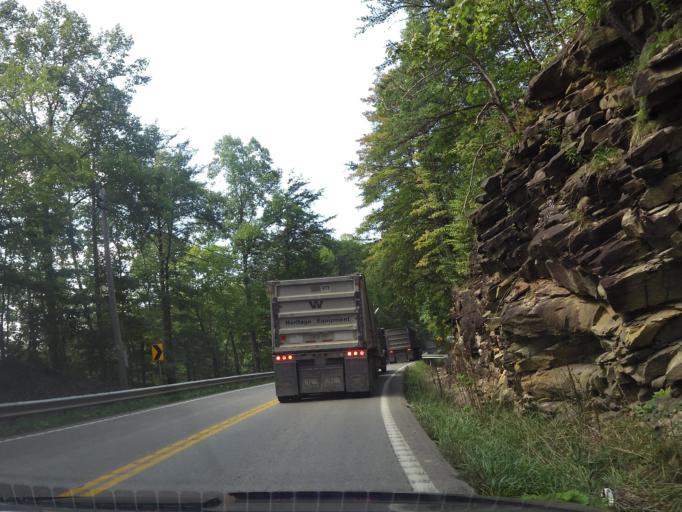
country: US
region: Kentucky
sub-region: Harlan County
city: Harlan
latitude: 36.8812
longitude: -83.3100
